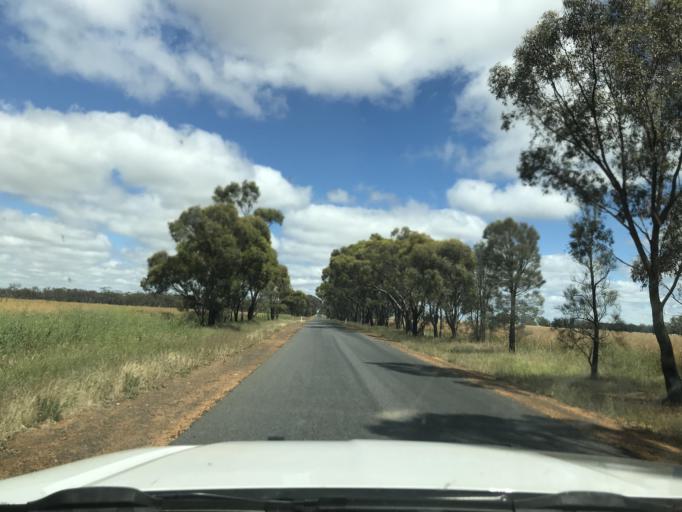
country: AU
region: South Australia
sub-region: Naracoorte and Lucindale
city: Naracoorte
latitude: -36.6833
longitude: 141.3122
